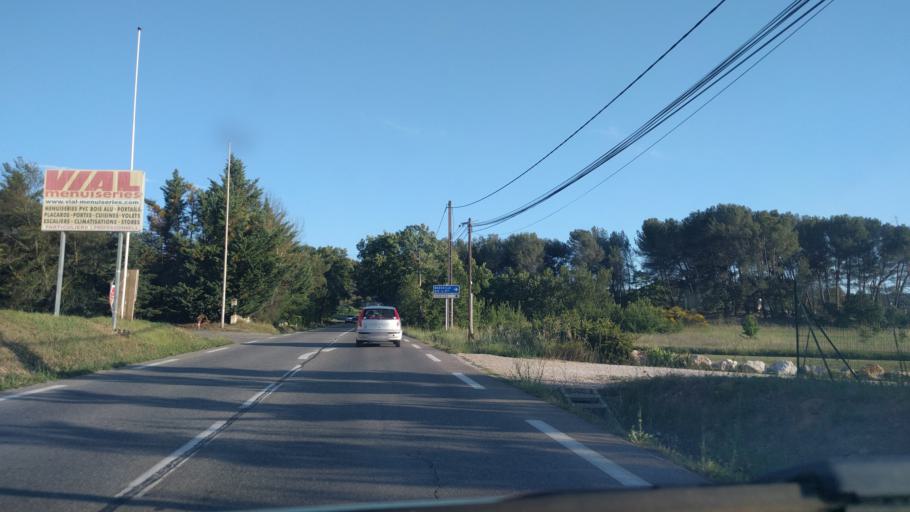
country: FR
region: Provence-Alpes-Cote d'Azur
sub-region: Departement des Bouches-du-Rhone
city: Venelles
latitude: 43.6111
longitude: 5.4955
